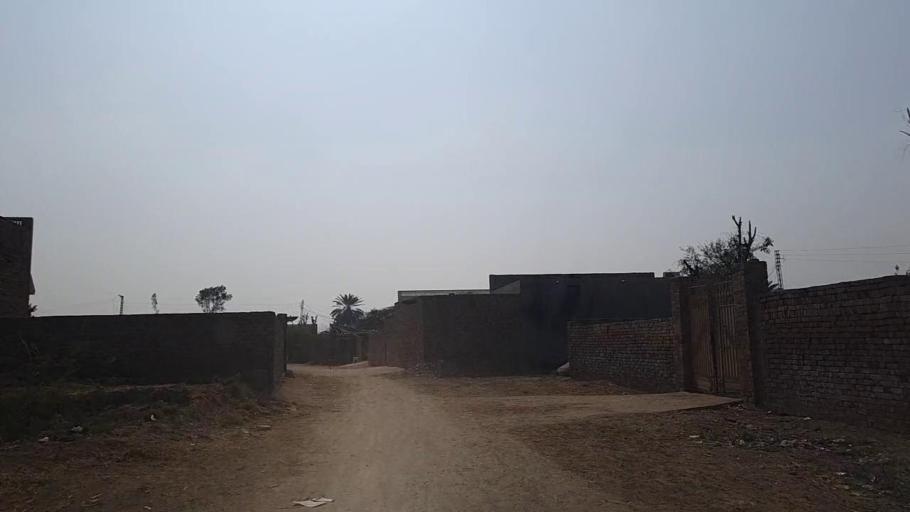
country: PK
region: Sindh
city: Daur
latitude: 26.4475
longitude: 68.4426
